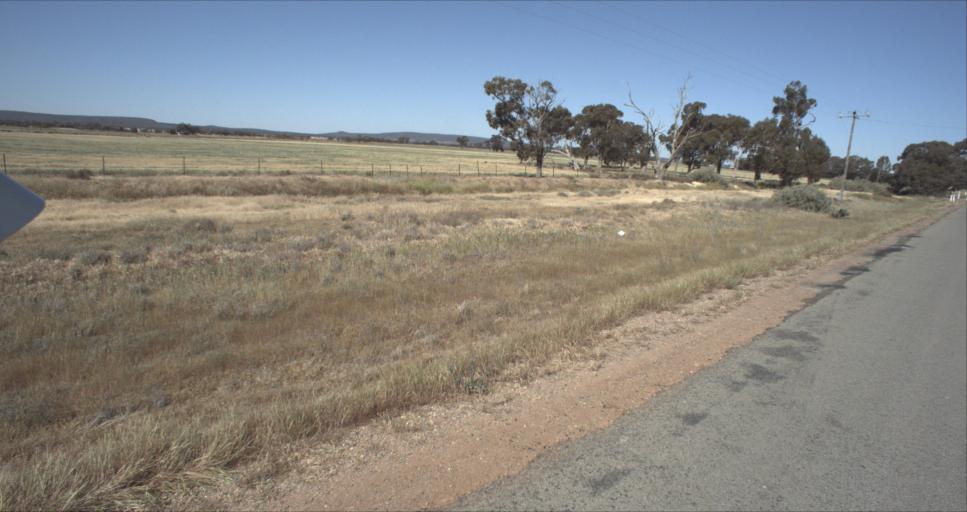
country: AU
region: New South Wales
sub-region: Leeton
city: Leeton
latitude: -34.4985
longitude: 146.3923
